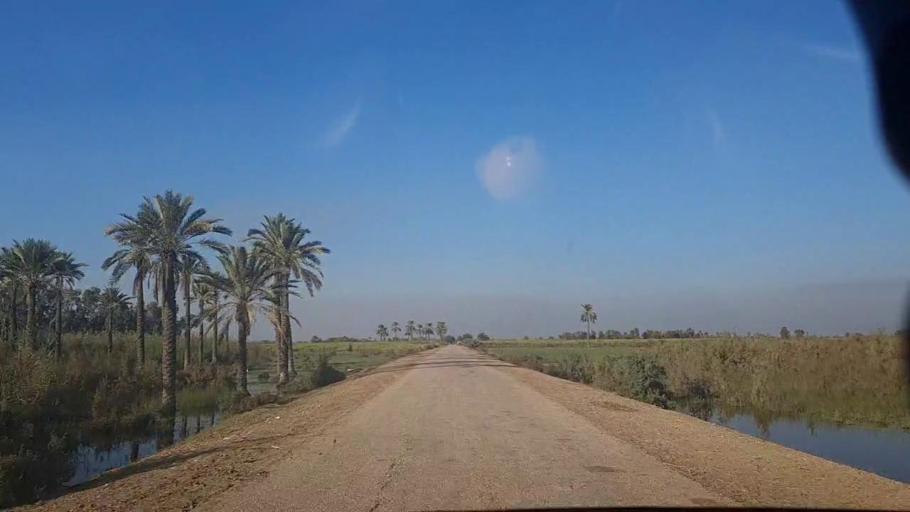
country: PK
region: Sindh
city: Sobhadero
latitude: 27.4076
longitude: 68.4222
